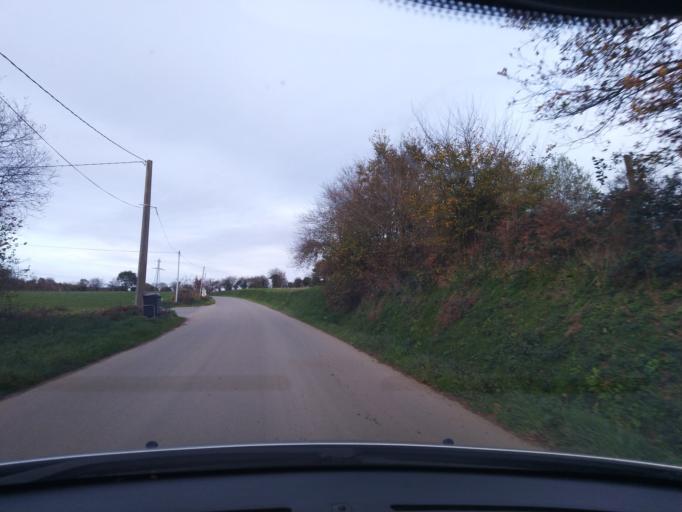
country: FR
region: Brittany
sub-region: Departement du Finistere
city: Guerlesquin
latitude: 48.5478
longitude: -3.6197
